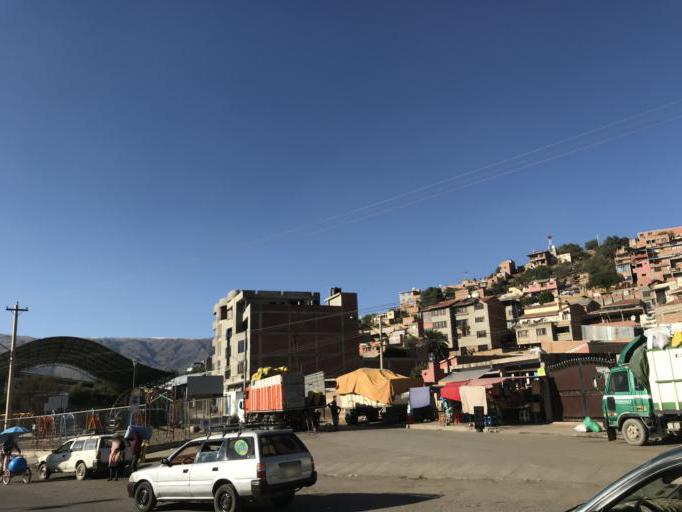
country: BO
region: Cochabamba
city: Cochabamba
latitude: -17.4177
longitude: -66.1516
